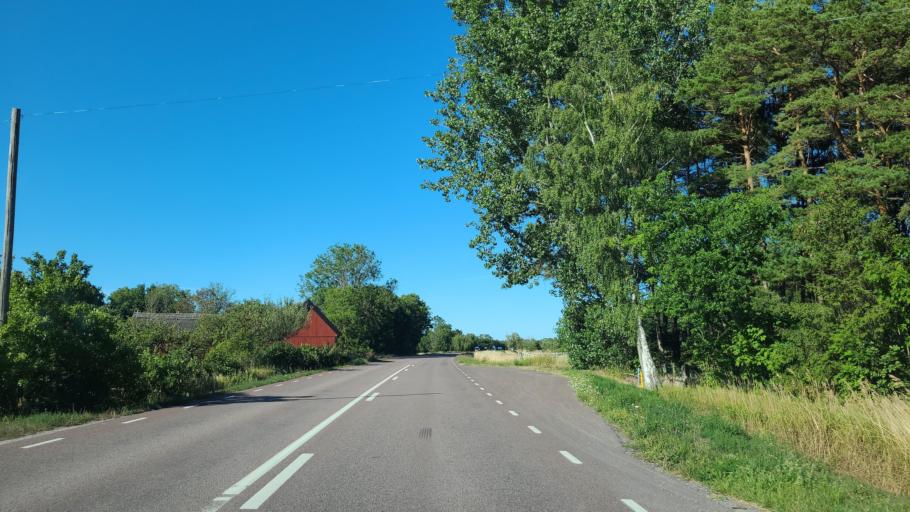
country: SE
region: Kalmar
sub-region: Borgholms Kommun
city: Borgholm
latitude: 57.1901
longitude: 17.0318
